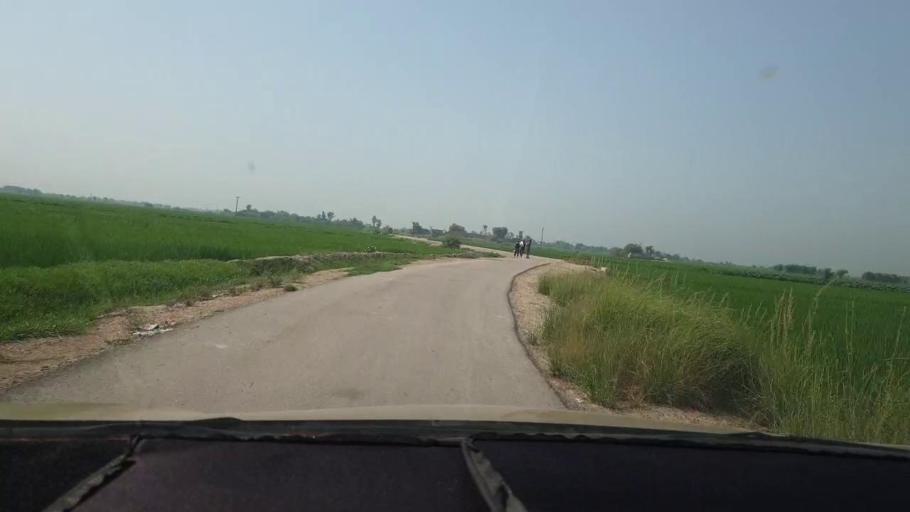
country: PK
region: Sindh
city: Kambar
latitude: 27.5652
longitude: 68.0445
